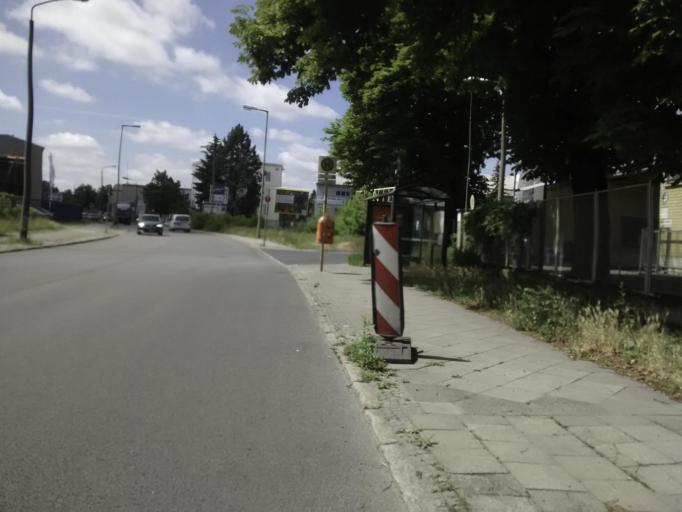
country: DE
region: Berlin
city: Niederschonhausen
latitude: 52.5905
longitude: 13.4162
